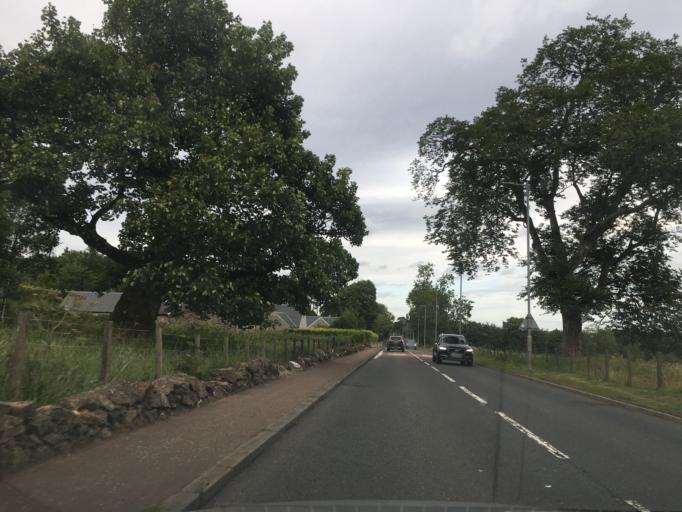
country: GB
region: Scotland
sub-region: The Scottish Borders
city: West Linton
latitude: 55.7027
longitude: -3.4297
